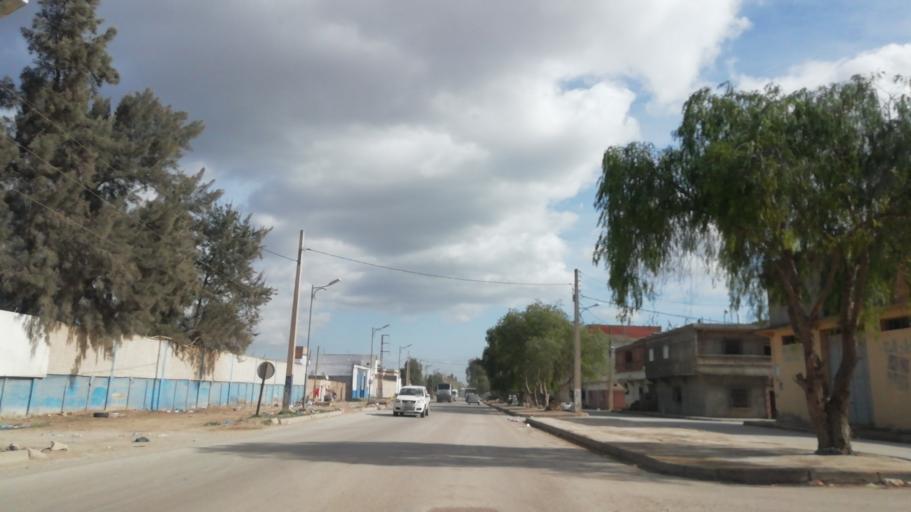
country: DZ
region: Oran
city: Es Senia
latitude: 35.6518
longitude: -0.5781
